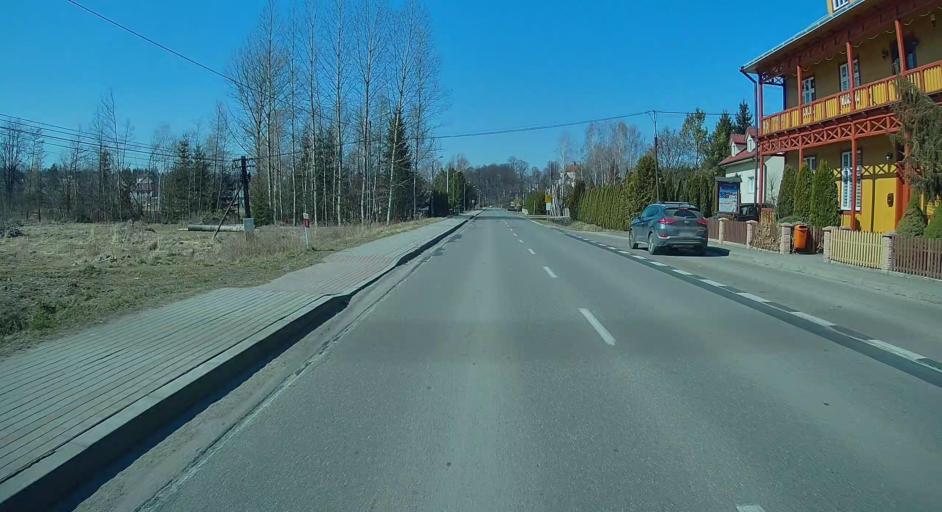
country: PL
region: Subcarpathian Voivodeship
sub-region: Powiat rzeszowski
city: Hyzne
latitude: 49.9204
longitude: 22.1734
